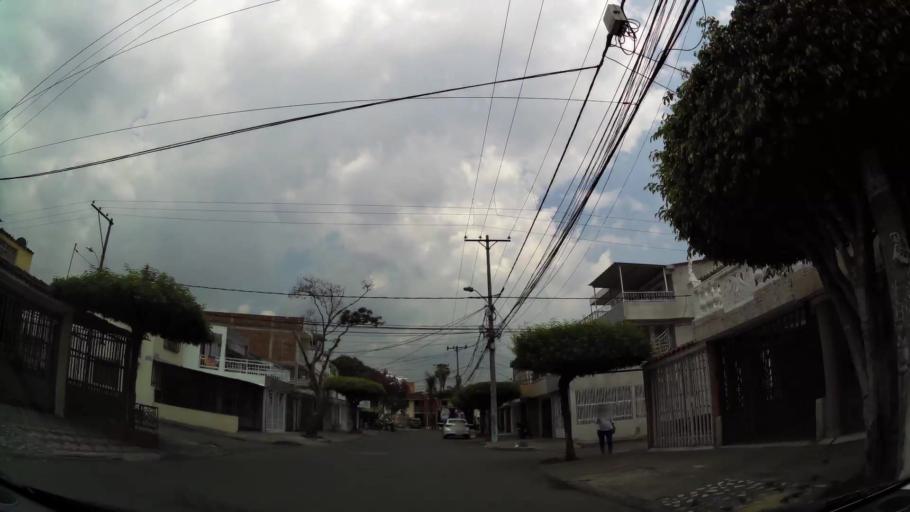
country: CO
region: Valle del Cauca
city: Cali
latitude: 3.4750
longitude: -76.5016
